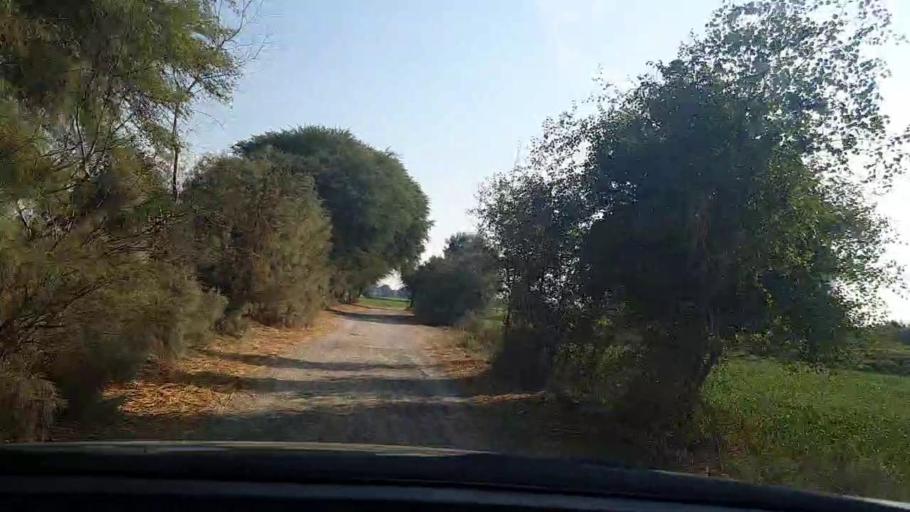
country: PK
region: Sindh
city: Sehwan
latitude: 26.3054
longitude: 68.0016
